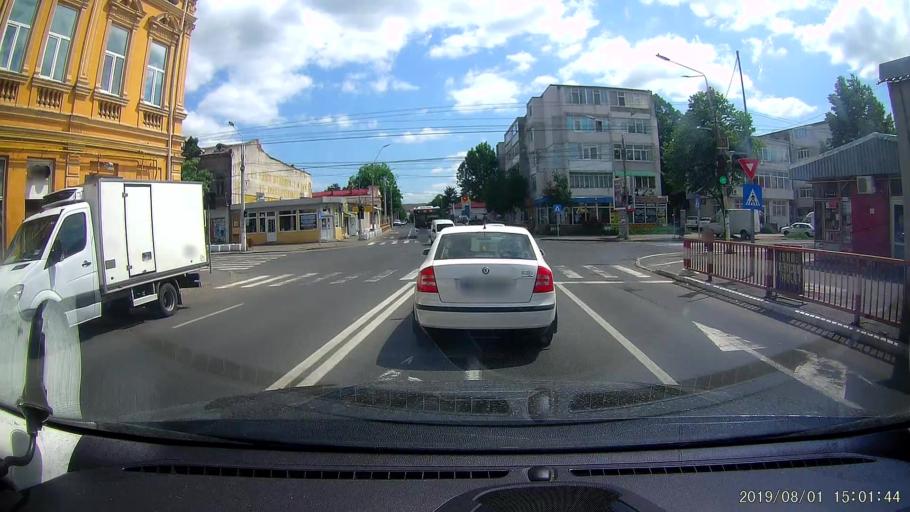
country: RO
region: Braila
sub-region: Municipiul Braila
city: Braila
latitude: 45.2716
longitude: 27.9603
